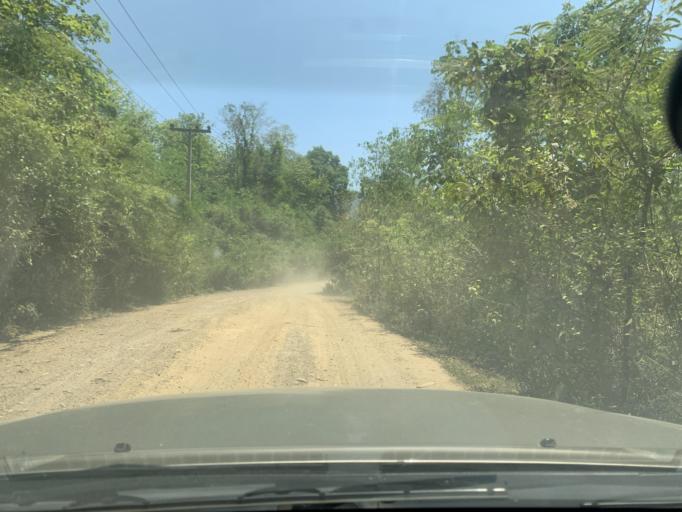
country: LA
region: Louangphabang
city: Louangphabang
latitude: 19.9069
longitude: 102.2367
